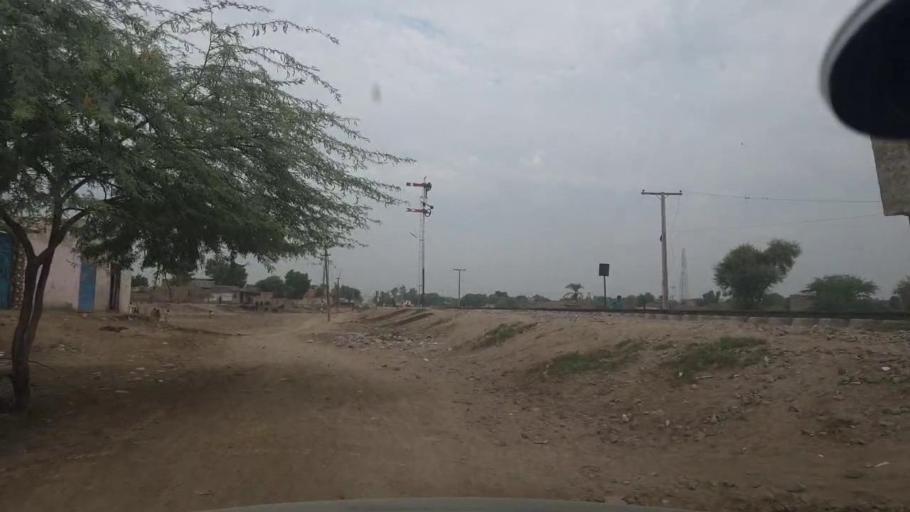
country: PK
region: Sindh
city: Jacobabad
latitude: 28.2670
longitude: 68.4428
